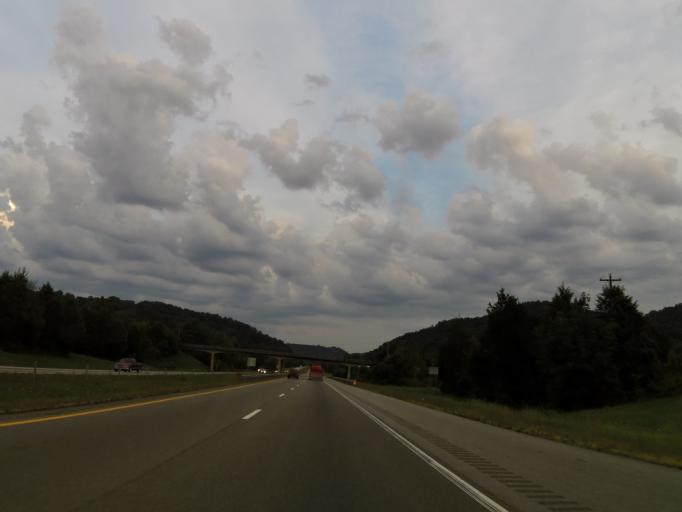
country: US
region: Tennessee
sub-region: Anderson County
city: Norris
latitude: 36.1503
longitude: -84.0643
